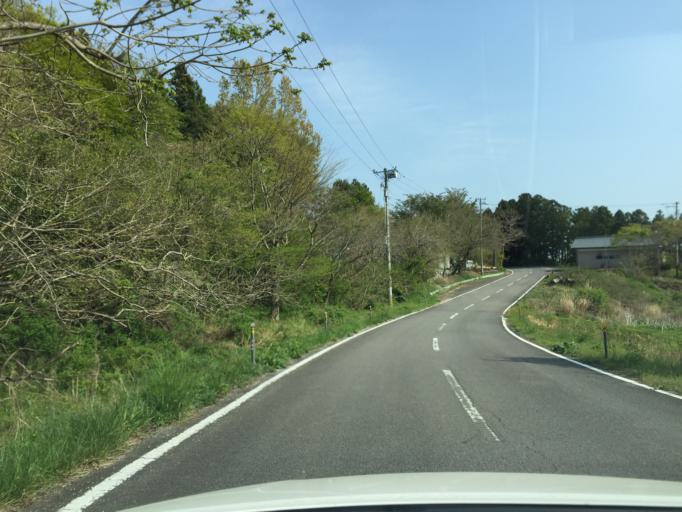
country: JP
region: Fukushima
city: Iwaki
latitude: 37.1567
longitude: 140.8556
